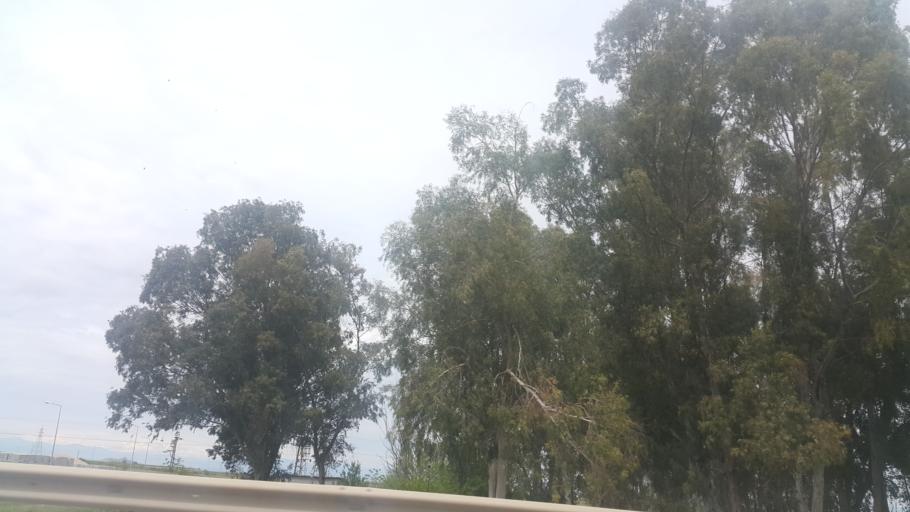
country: TR
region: Adana
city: Ceyhan
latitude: 37.0531
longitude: 35.7828
